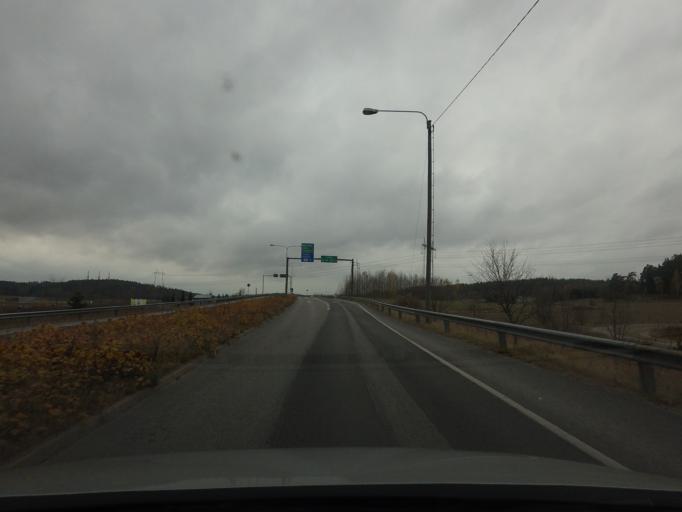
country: FI
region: Varsinais-Suomi
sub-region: Turku
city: Paimio
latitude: 60.4447
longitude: 22.6044
